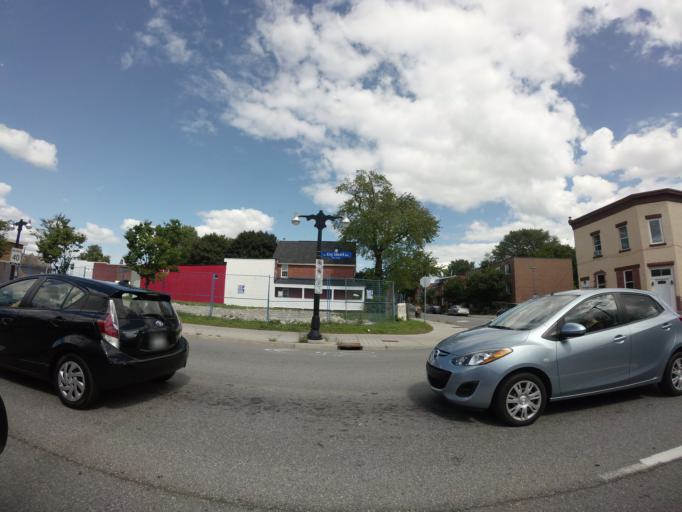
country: CA
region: Ontario
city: Ottawa
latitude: 45.4314
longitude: -75.6879
